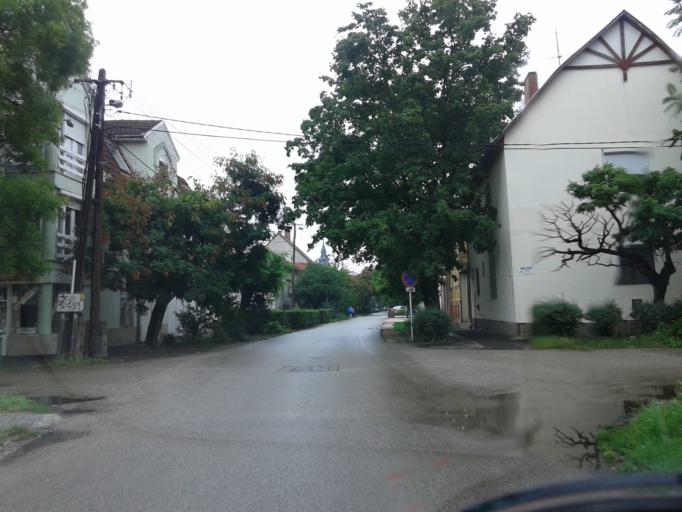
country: HU
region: Csongrad
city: Szeged
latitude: 46.2428
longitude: 20.1315
